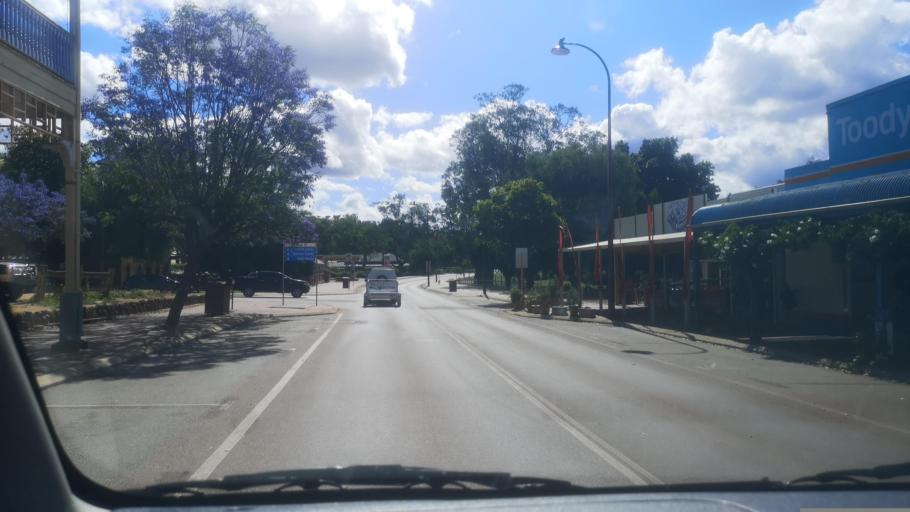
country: AU
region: Western Australia
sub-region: Toodyay
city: Toodyay
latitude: -31.5502
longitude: 116.4660
